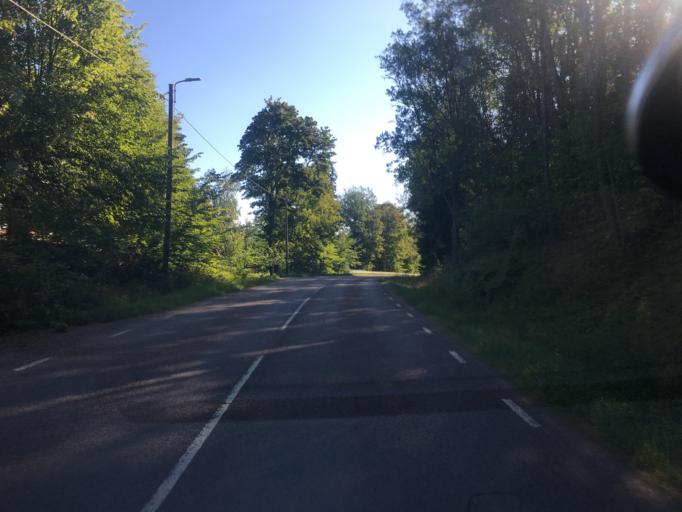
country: SE
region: Vaestmanland
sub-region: Vasteras
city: Tillberga
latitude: 59.6998
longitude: 16.6371
